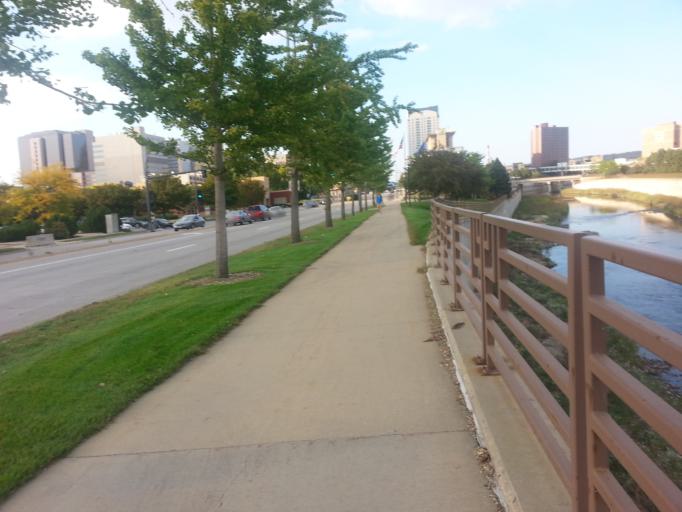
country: US
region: Minnesota
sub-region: Olmsted County
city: Rochester
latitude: 44.0164
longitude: -92.4628
